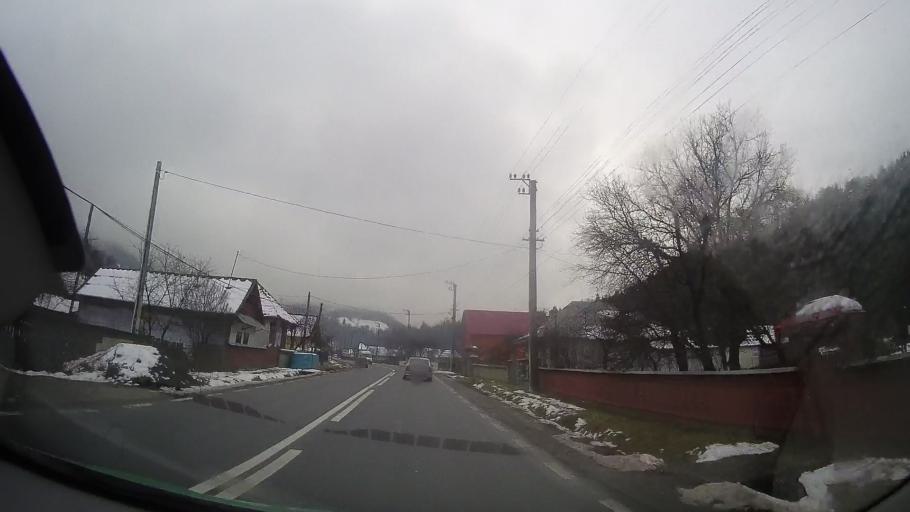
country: RO
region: Neamt
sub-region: Comuna Bicazu Ardelean
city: Bicazu Ardelean
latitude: 46.8622
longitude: 25.9372
